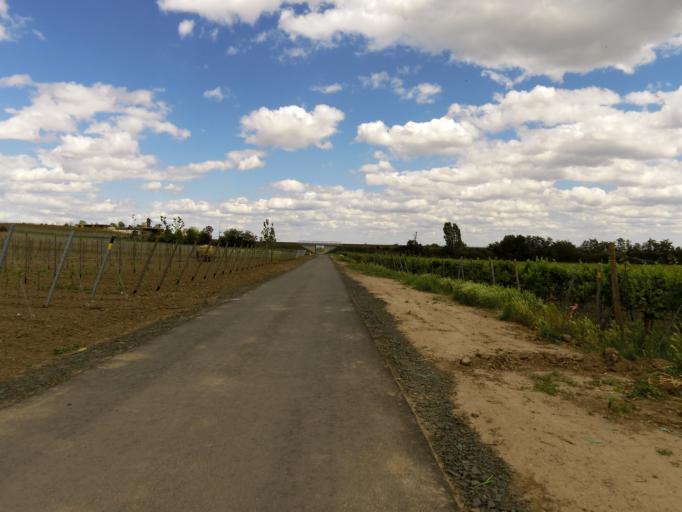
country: DE
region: Rheinland-Pfalz
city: Freinsheim
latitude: 49.4952
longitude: 8.2056
